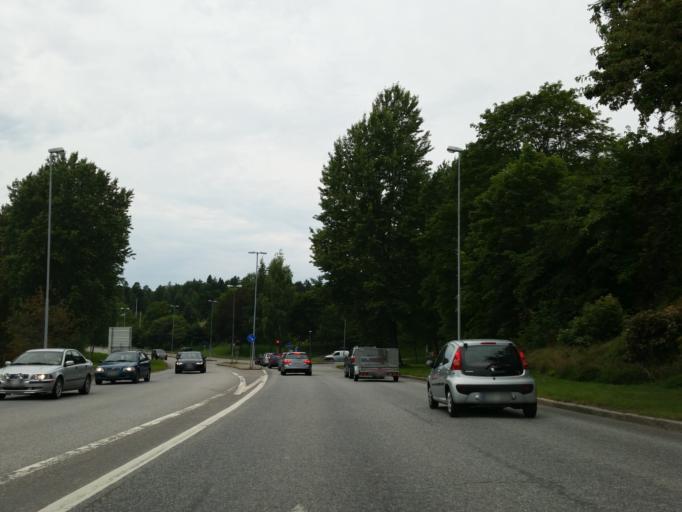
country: SE
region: Stockholm
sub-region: Sodertalje Kommun
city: Soedertaelje
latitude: 59.2029
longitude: 17.6046
